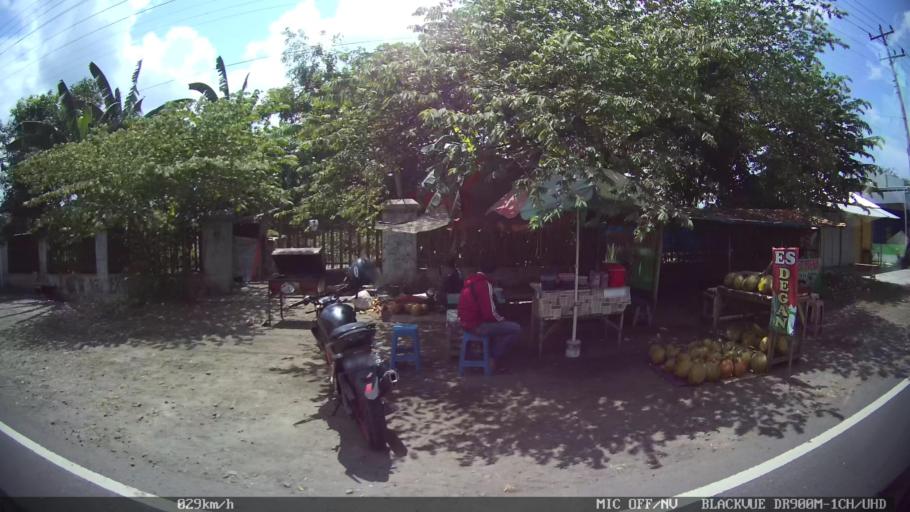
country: ID
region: Daerah Istimewa Yogyakarta
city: Bantul
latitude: -7.8812
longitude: 110.3405
